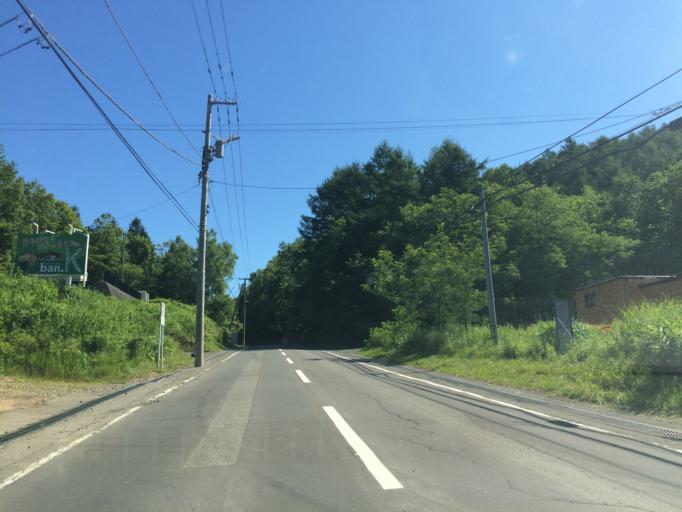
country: JP
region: Hokkaido
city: Sapporo
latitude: 43.0356
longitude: 141.2842
